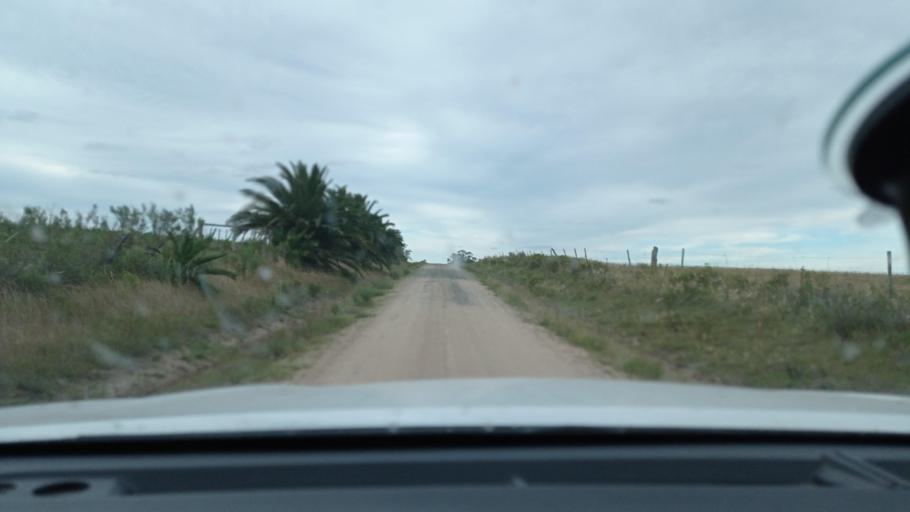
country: UY
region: Florida
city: Casupa
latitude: -34.1336
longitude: -55.7806
